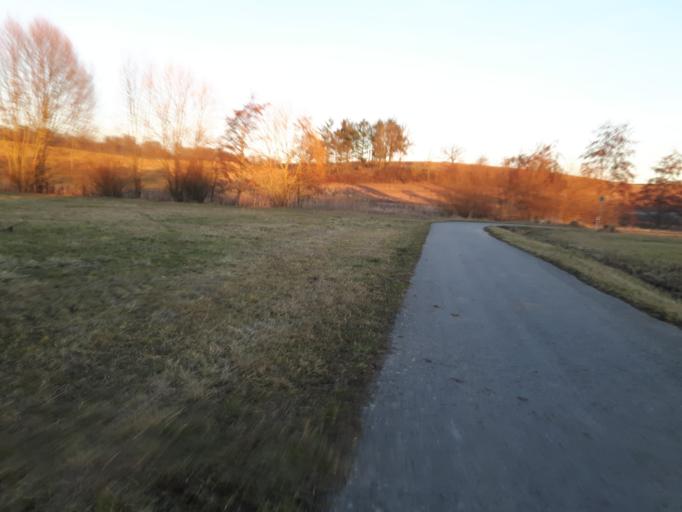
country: DE
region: Baden-Wuerttemberg
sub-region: Regierungsbezirk Stuttgart
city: Massenbachhausen
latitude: 49.1814
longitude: 9.0548
